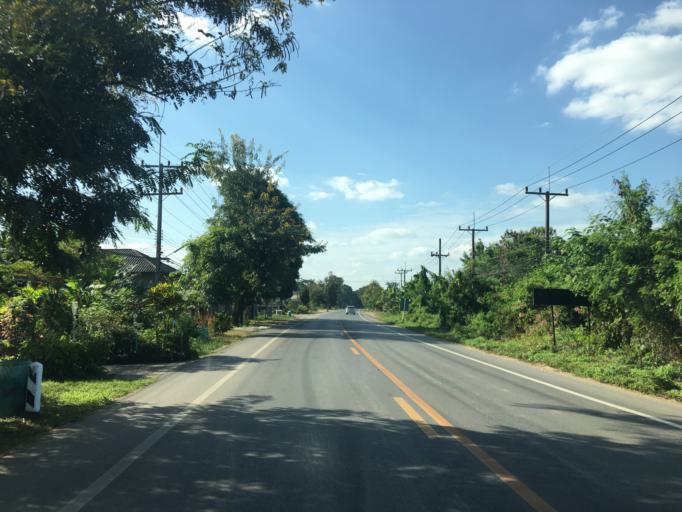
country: TH
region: Phayao
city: Chun
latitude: 19.3451
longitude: 100.1177
